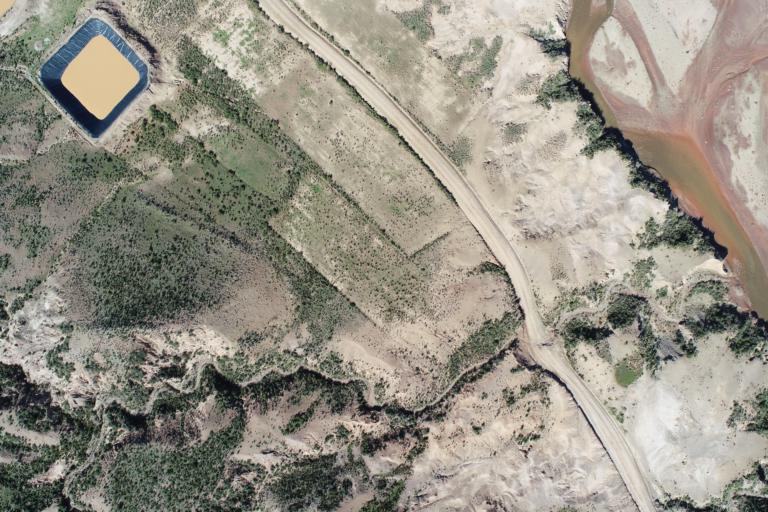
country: BO
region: La Paz
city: Curahuara de Carangas
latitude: -17.3041
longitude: -68.4937
